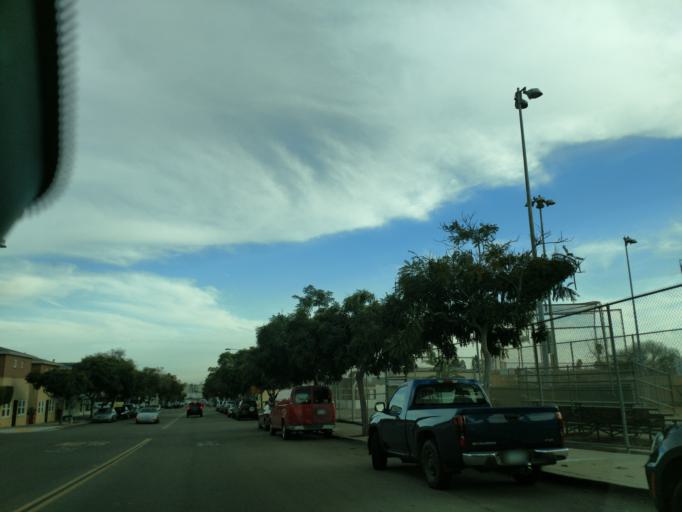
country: US
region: California
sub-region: San Diego County
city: Coronado
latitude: 32.7223
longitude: -117.2332
